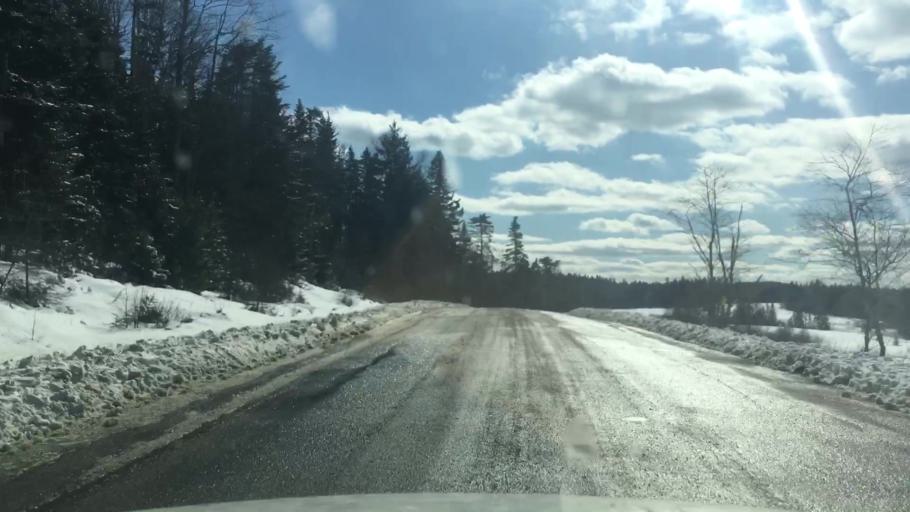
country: US
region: Maine
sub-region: Washington County
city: Machiasport
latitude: 44.6723
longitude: -67.4227
